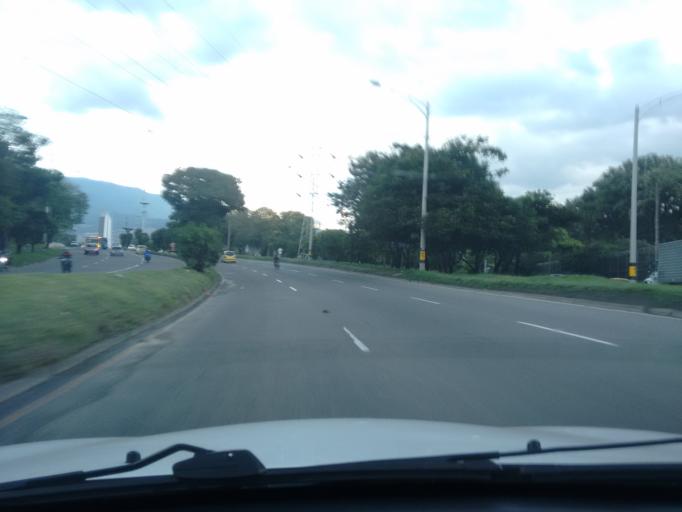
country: CO
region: Antioquia
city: Medellin
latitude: 6.2628
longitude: -75.5750
